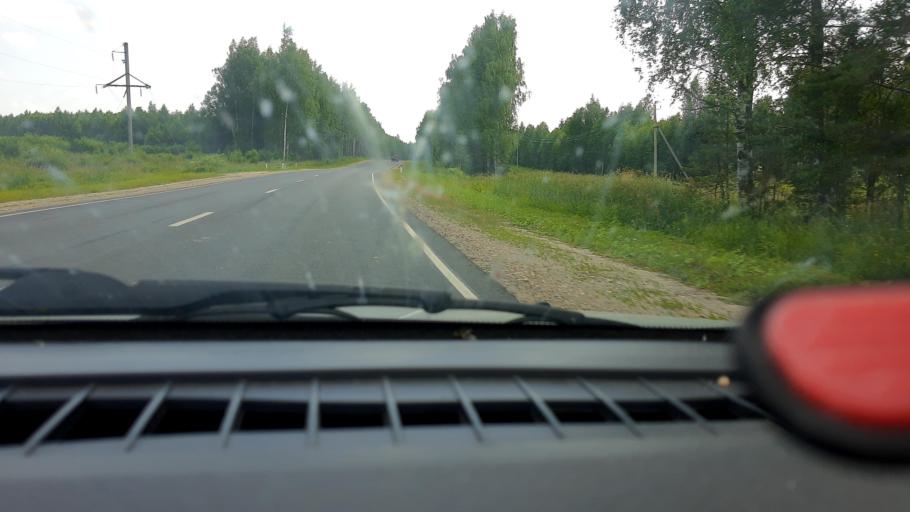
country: RU
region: Nizjnij Novgorod
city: Krasnyye Baki
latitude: 57.0539
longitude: 45.1363
